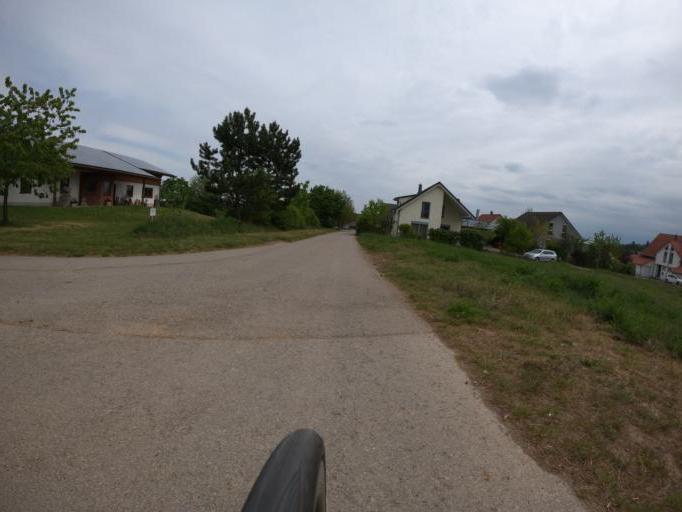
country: DE
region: Baden-Wuerttemberg
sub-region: Regierungsbezirk Stuttgart
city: Aidlingen
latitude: 48.7022
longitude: 8.8875
